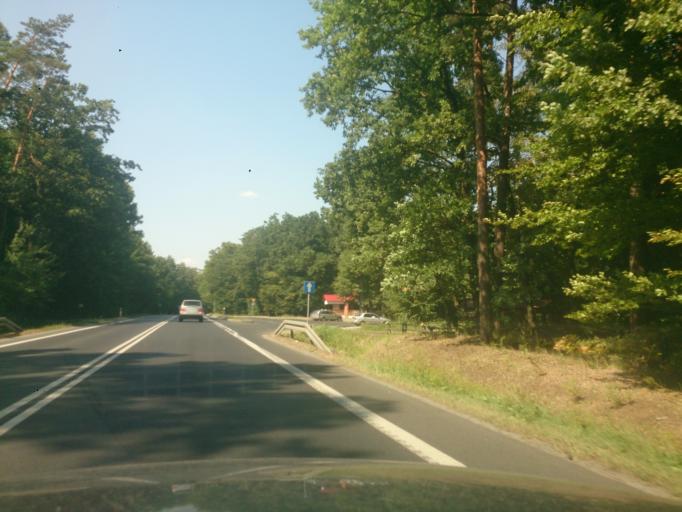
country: PL
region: Subcarpathian Voivodeship
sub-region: Powiat rzeszowski
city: Glogow Malopolski
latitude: 50.1747
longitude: 21.9324
